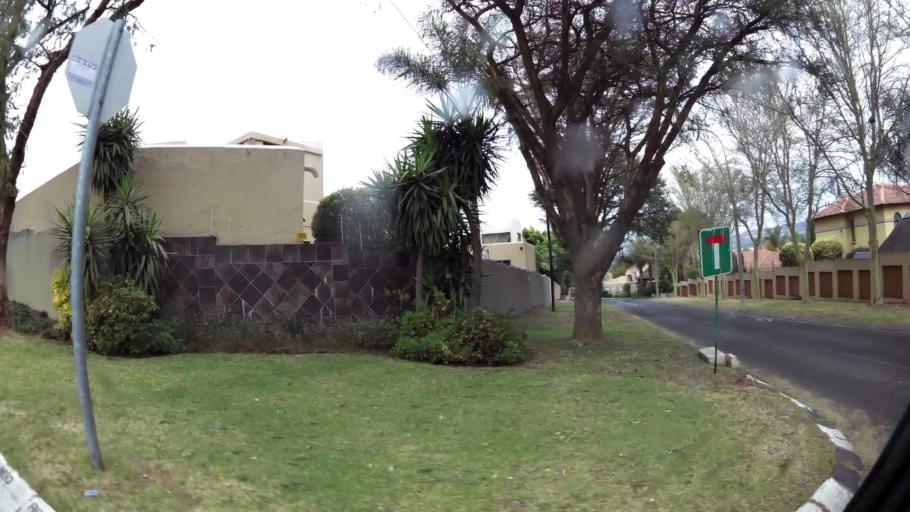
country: ZA
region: Gauteng
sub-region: City of Johannesburg Metropolitan Municipality
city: Roodepoort
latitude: -26.1166
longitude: 27.9137
